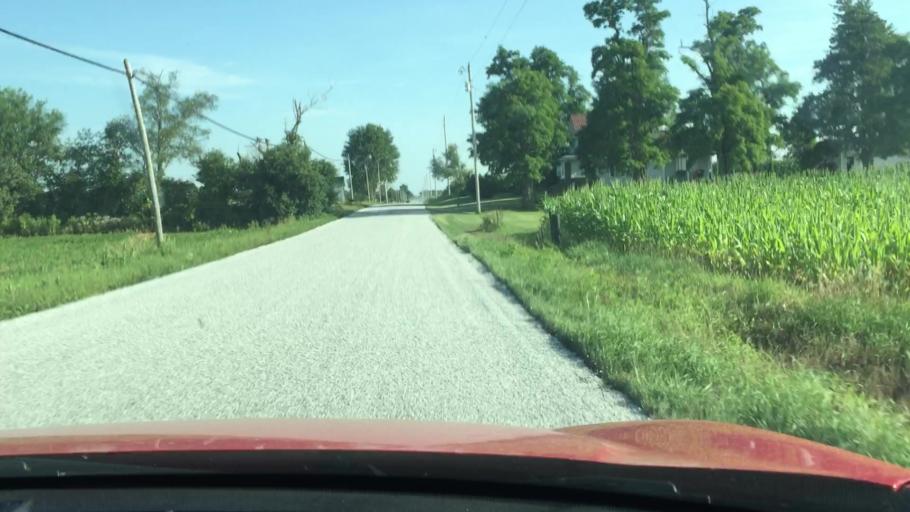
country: US
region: Ohio
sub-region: Hardin County
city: Ada
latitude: 40.7552
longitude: -83.8424
